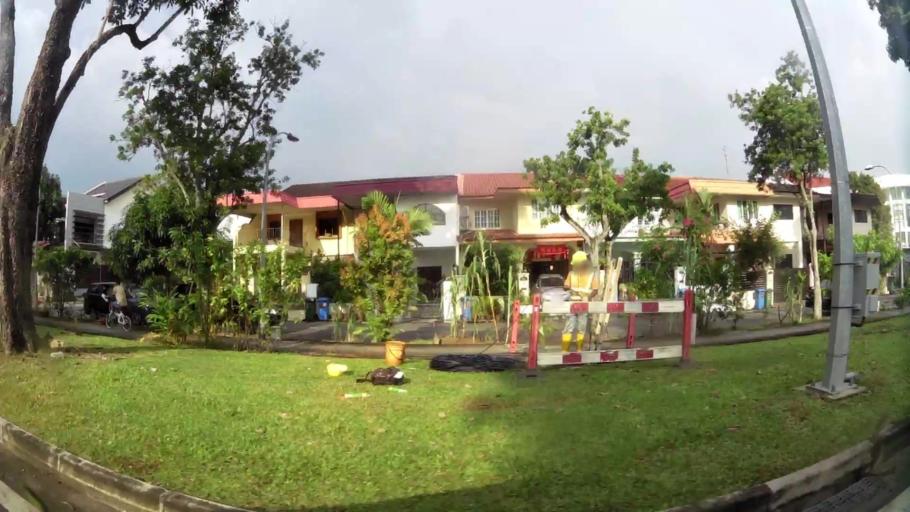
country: SG
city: Singapore
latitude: 1.3239
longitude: 103.9534
